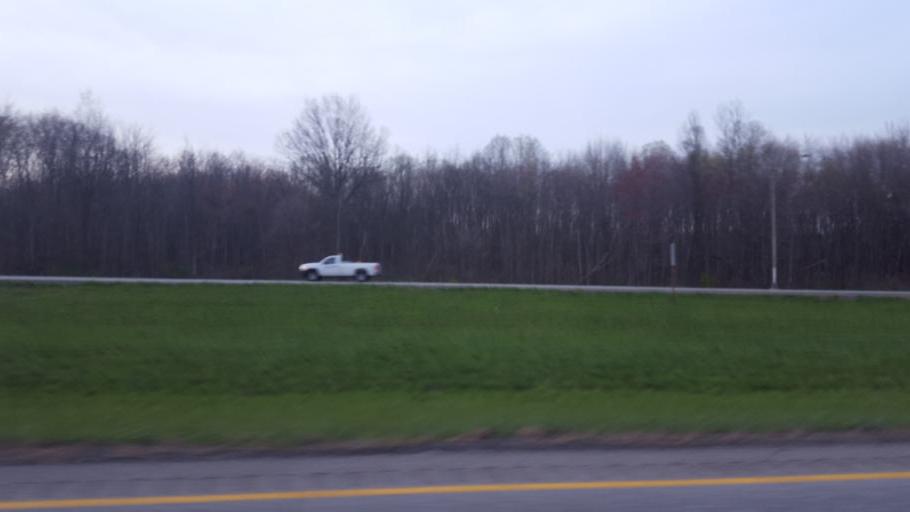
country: US
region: Ohio
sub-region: Lorain County
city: Sheffield
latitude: 41.4032
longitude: -82.1386
